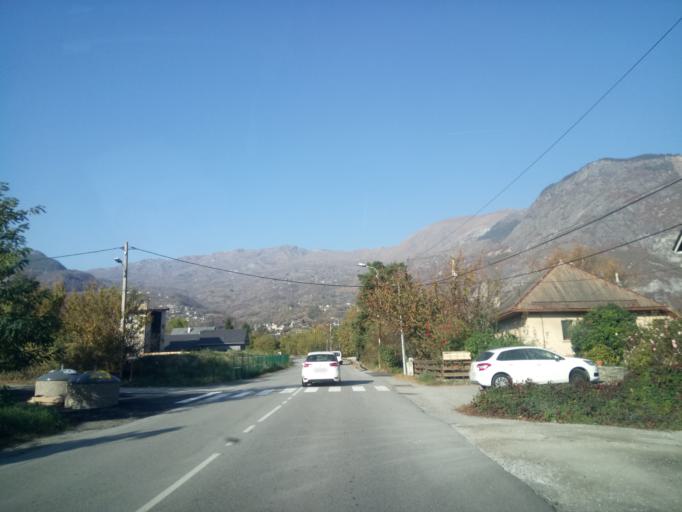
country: FR
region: Rhone-Alpes
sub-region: Departement de la Savoie
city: Villargondran
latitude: 45.2702
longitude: 6.3593
